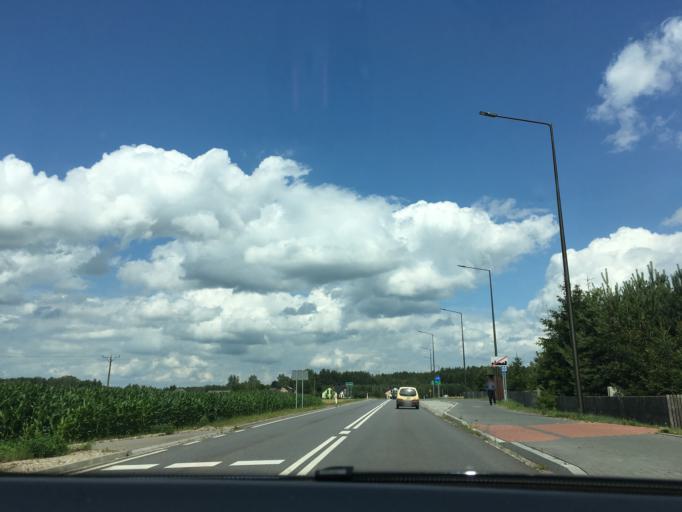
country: PL
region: Podlasie
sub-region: Powiat sejnenski
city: Krasnopol
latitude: 54.0877
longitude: 23.1271
